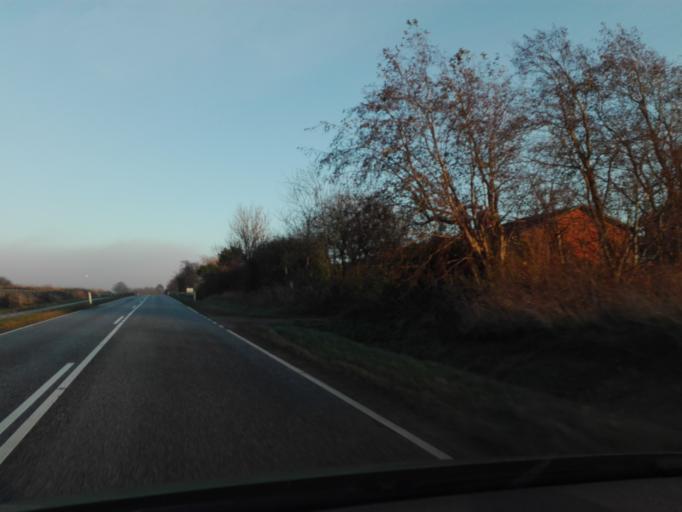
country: DK
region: Central Jutland
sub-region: Skanderborg Kommune
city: Galten
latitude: 56.1808
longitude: 9.9142
